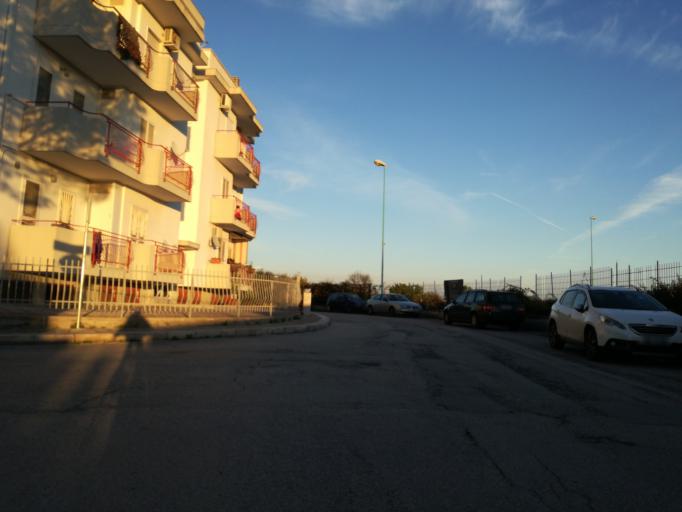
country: IT
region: Apulia
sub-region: Provincia di Bari
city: Adelfia
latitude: 40.9987
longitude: 16.8777
